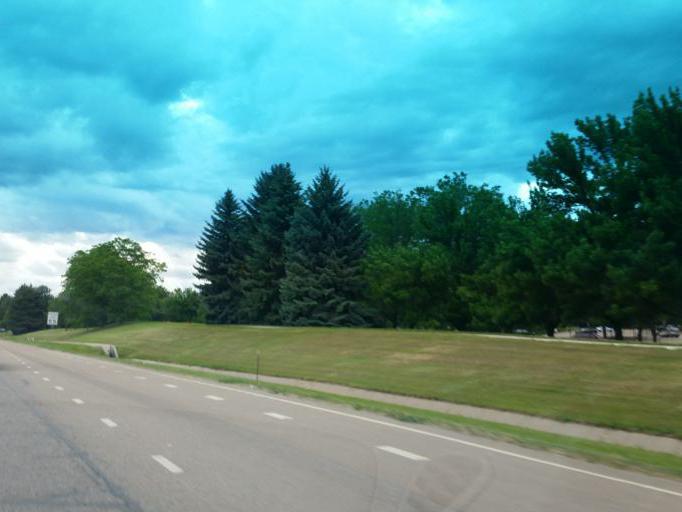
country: US
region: Colorado
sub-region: Larimer County
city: Fort Collins
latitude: 40.5235
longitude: -105.0122
